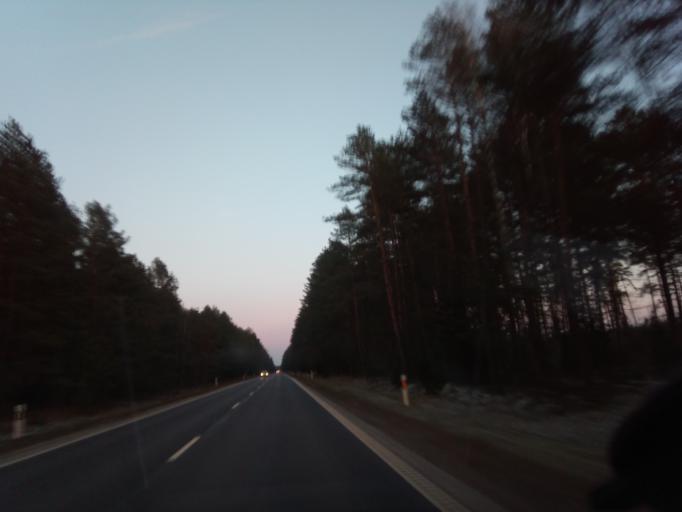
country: LT
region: Vilnius County
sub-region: Trakai
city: Rudiskes
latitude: 54.3808
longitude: 24.9262
